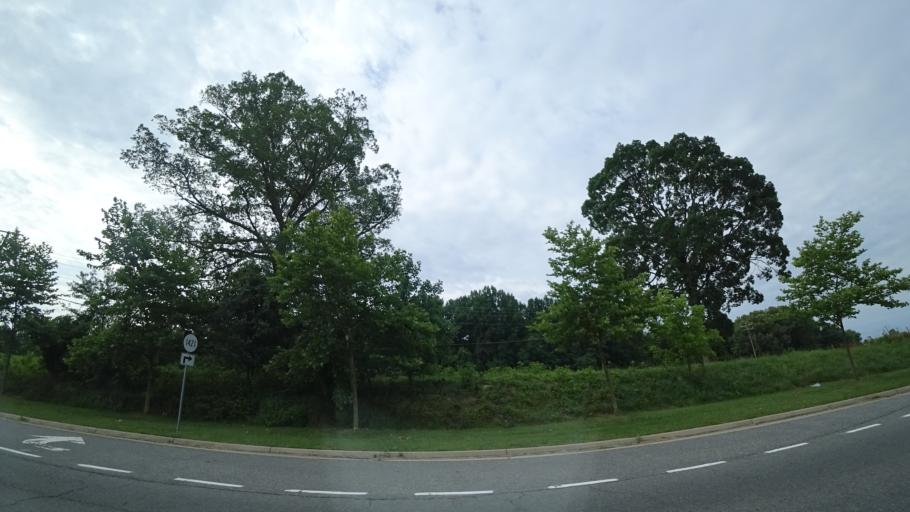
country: US
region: Virginia
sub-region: Spotsylvania County
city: Spotsylvania
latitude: 38.2085
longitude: -77.5797
